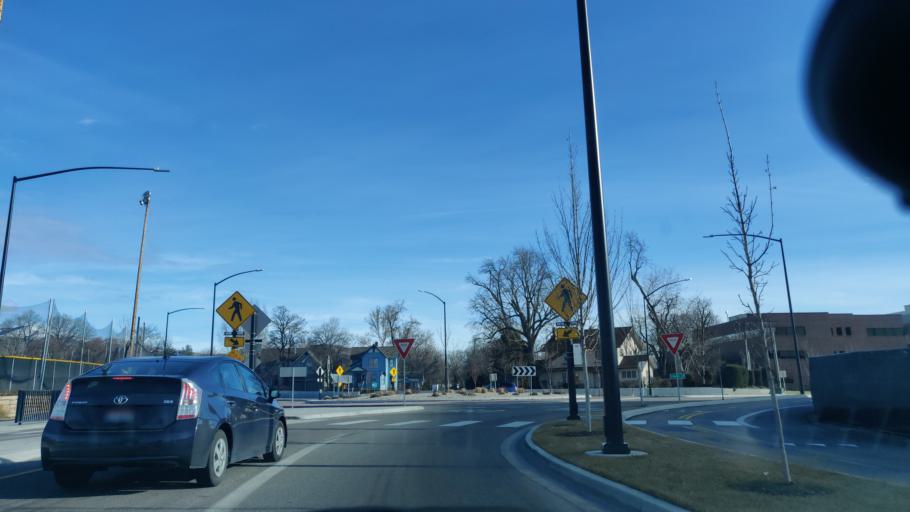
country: US
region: Idaho
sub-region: Ada County
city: Boise
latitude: 43.6139
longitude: -116.1912
